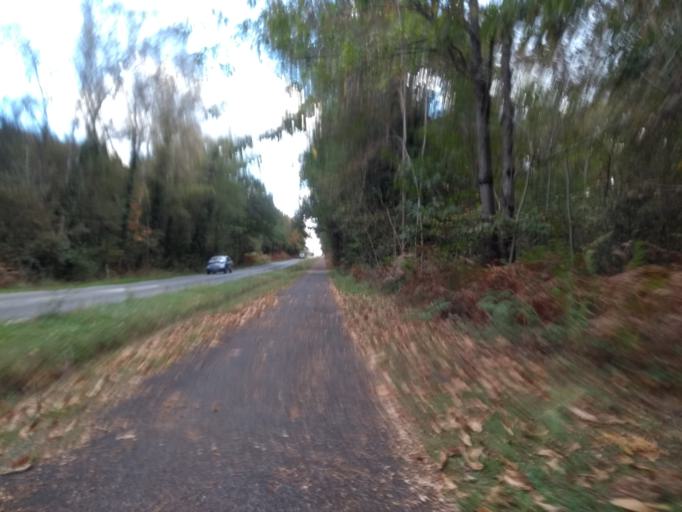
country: FR
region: Aquitaine
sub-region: Departement de la Gironde
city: Cestas
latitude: 44.7337
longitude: -0.6868
